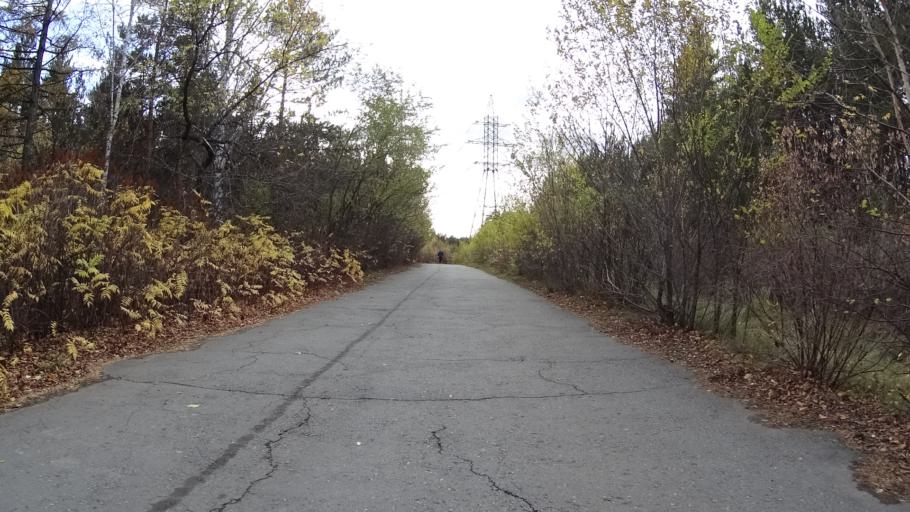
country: RU
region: Chelyabinsk
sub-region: Gorod Chelyabinsk
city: Chelyabinsk
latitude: 55.1565
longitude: 61.3541
